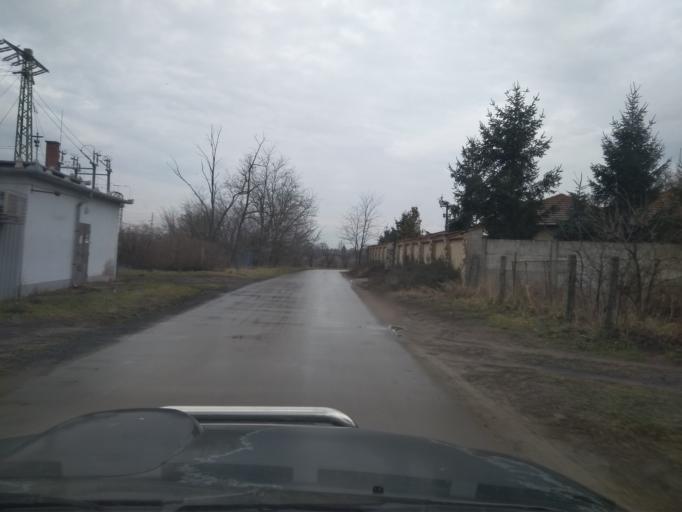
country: HU
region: Szabolcs-Szatmar-Bereg
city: Nyiregyhaza
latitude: 47.9662
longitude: 21.6855
